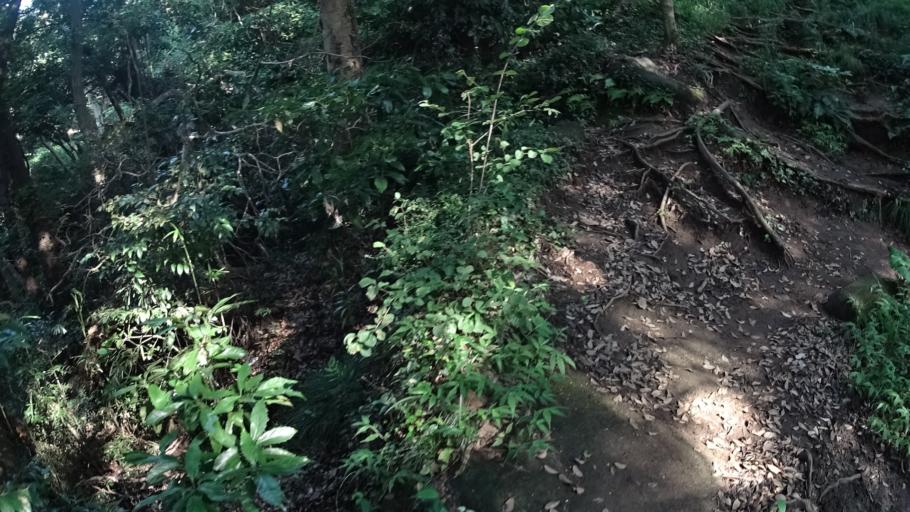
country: JP
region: Kanagawa
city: Zushi
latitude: 35.3055
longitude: 139.6139
